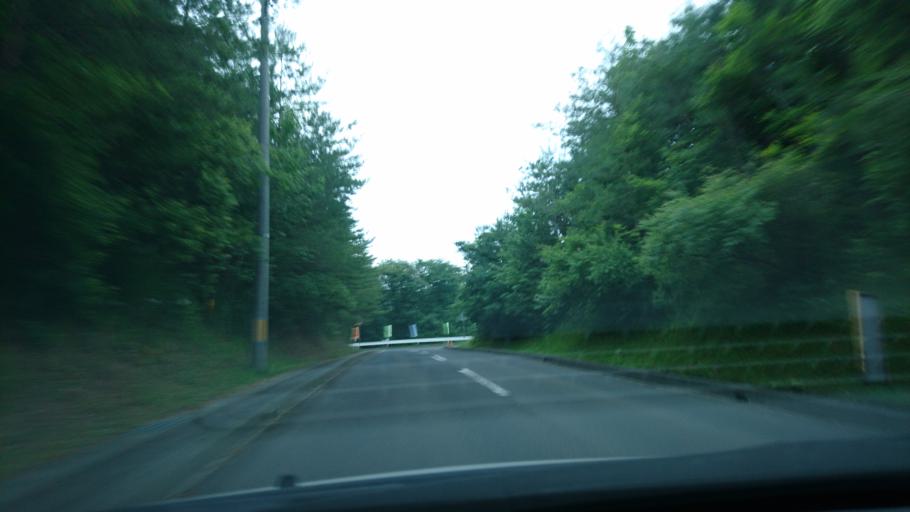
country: JP
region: Iwate
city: Ichinoseki
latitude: 38.9064
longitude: 141.1428
